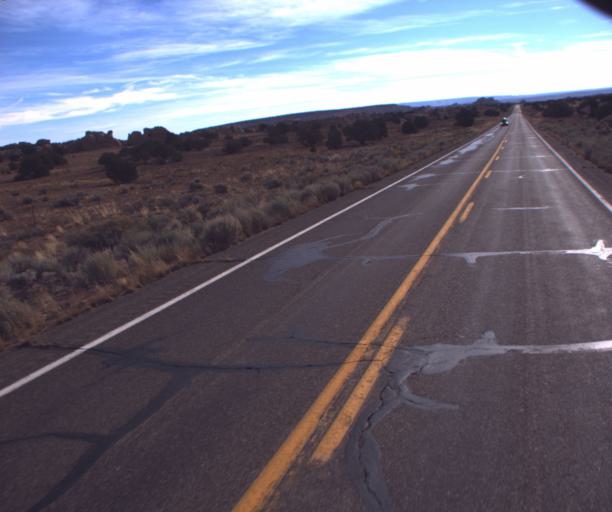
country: US
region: Arizona
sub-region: Coconino County
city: Kaibito
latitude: 36.6504
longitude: -111.2349
